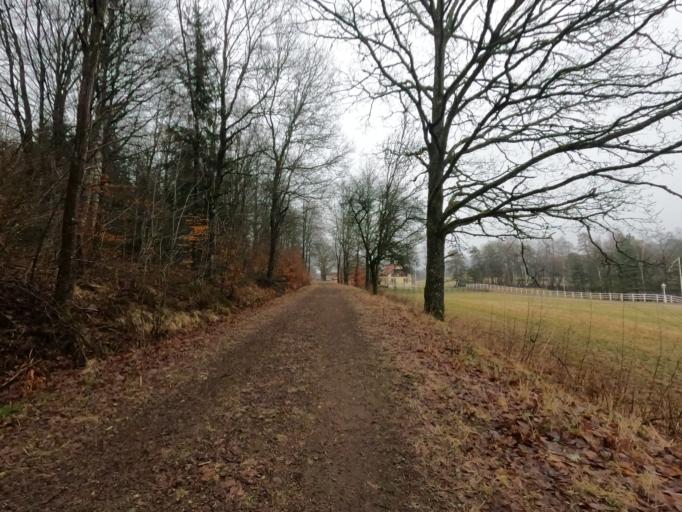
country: SE
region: Halland
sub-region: Halmstads Kommun
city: Oskarstrom
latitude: 56.7457
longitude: 13.1670
